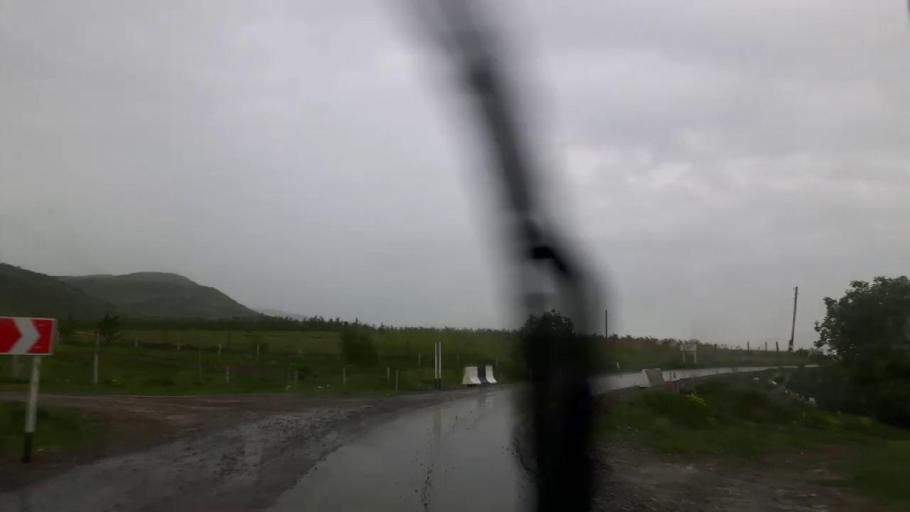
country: GE
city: Agara
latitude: 41.9823
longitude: 43.9526
